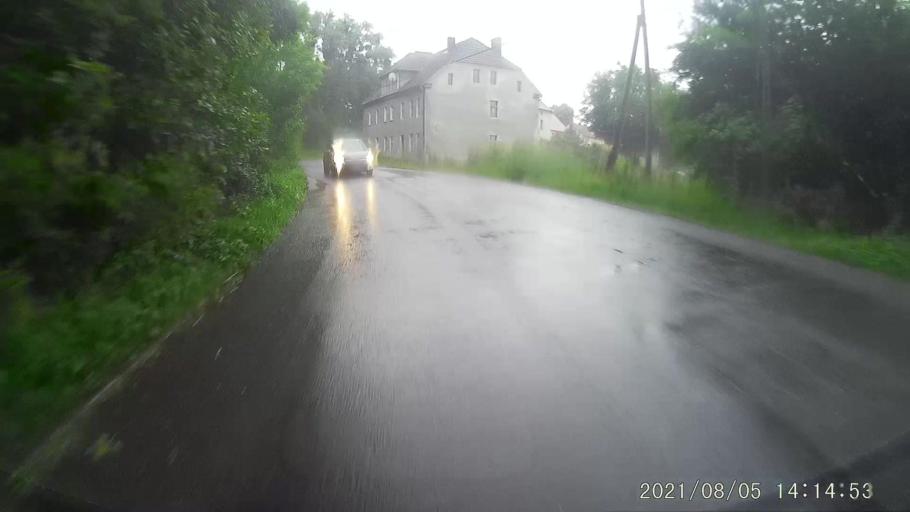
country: PL
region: Opole Voivodeship
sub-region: Powiat prudnicki
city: Biala
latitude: 50.4656
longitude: 17.7383
